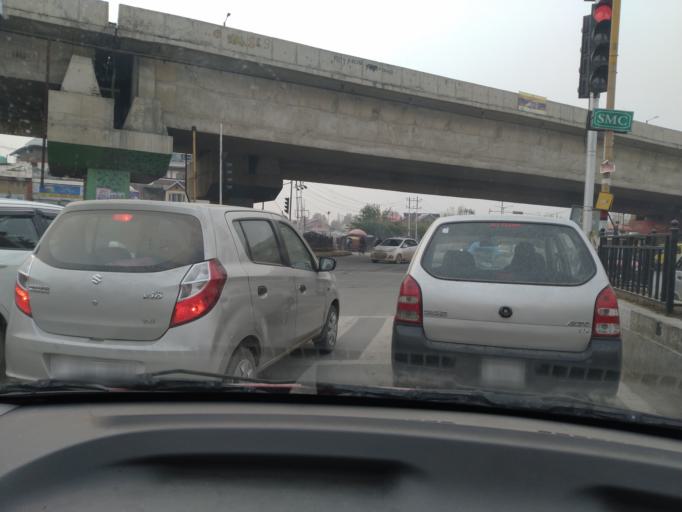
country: IN
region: Kashmir
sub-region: Srinagar
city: Srinagar
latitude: 34.0376
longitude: 74.7907
